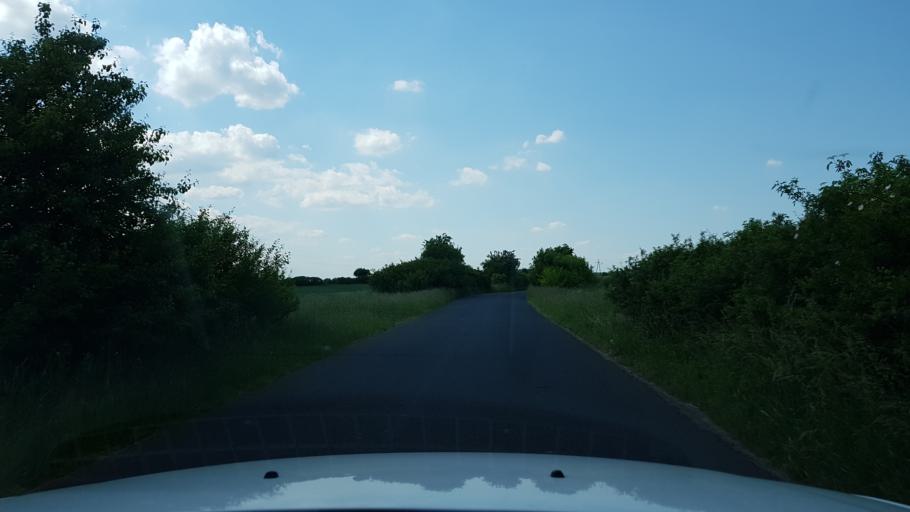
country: PL
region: West Pomeranian Voivodeship
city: Trzcinsko Zdroj
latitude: 52.9922
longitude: 14.5878
